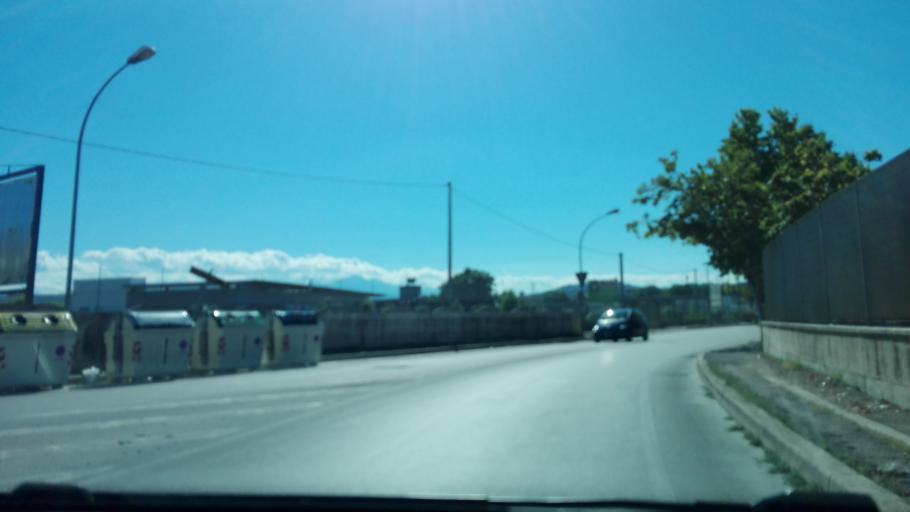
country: IT
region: Abruzzo
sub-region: Provincia di Pescara
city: Montesilvano Marina
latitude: 42.5128
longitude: 14.1405
